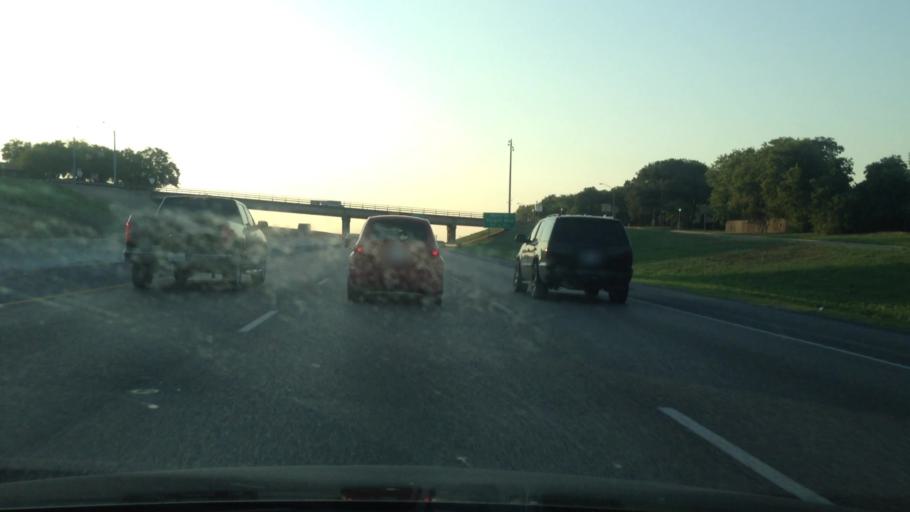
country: US
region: Texas
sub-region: Tarrant County
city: Forest Hill
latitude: 32.7071
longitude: -97.2708
